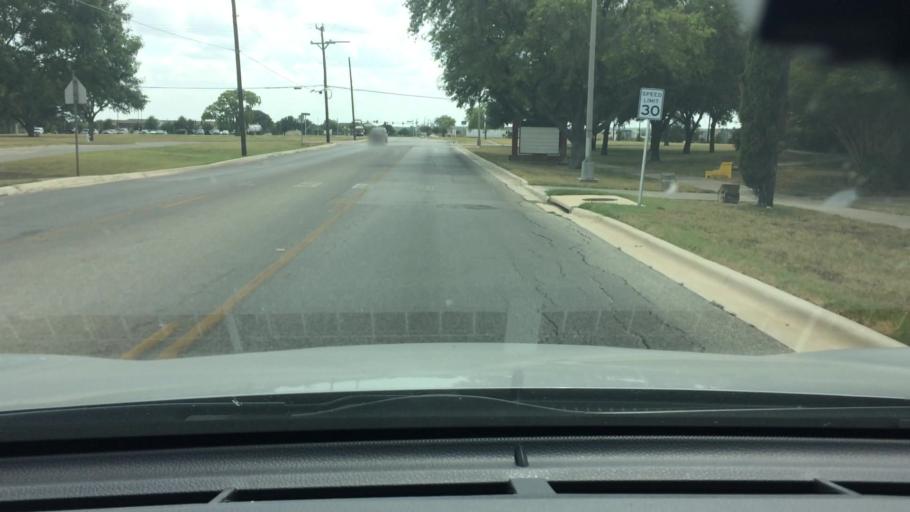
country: US
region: Texas
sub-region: Bexar County
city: San Antonio
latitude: 29.3476
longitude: -98.4418
